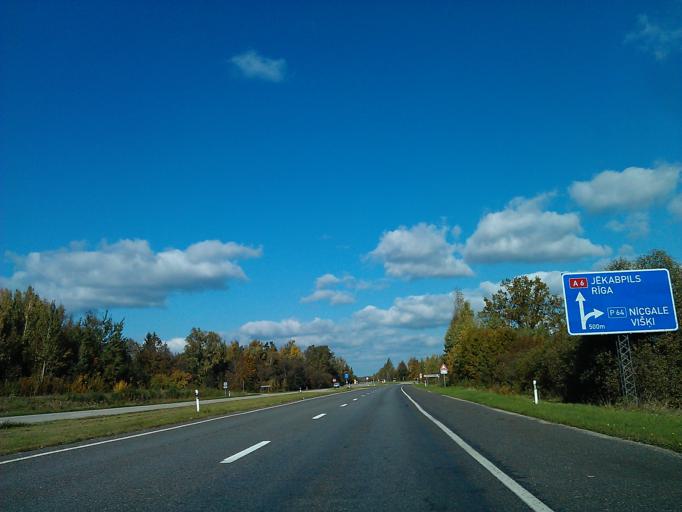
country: LV
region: Ilukste
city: Ilukste
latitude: 56.1374
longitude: 26.3436
